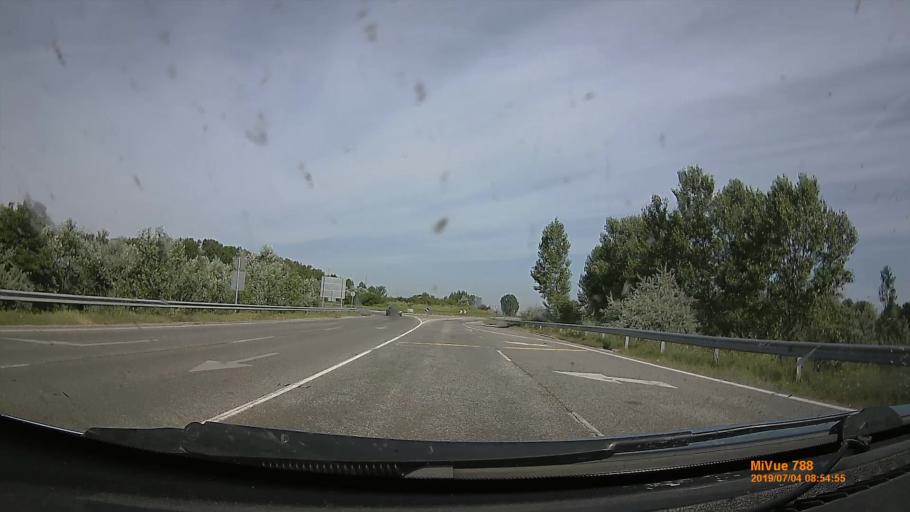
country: HU
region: Pest
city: Vecses
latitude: 47.3789
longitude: 19.2605
